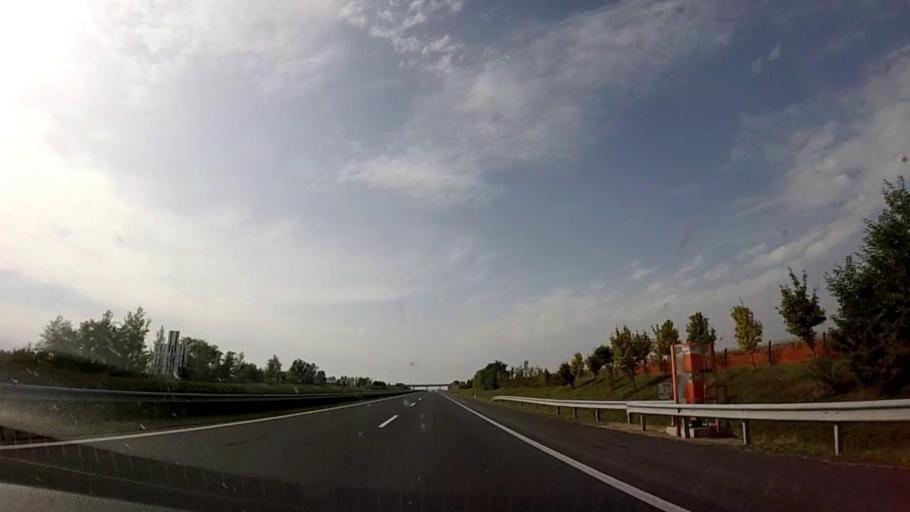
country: HU
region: Zala
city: Becsehely
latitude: 46.4371
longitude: 16.8014
